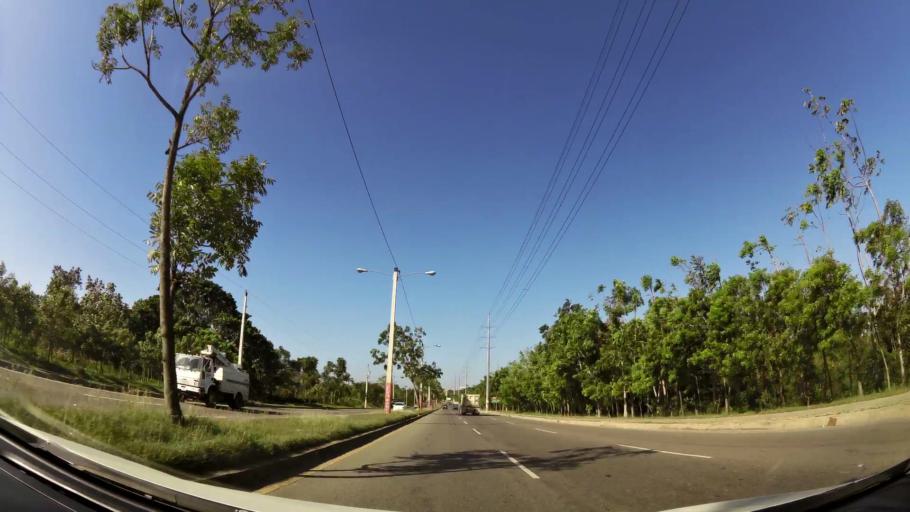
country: DO
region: San Cristobal
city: El Carril
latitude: 18.4473
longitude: -69.9959
